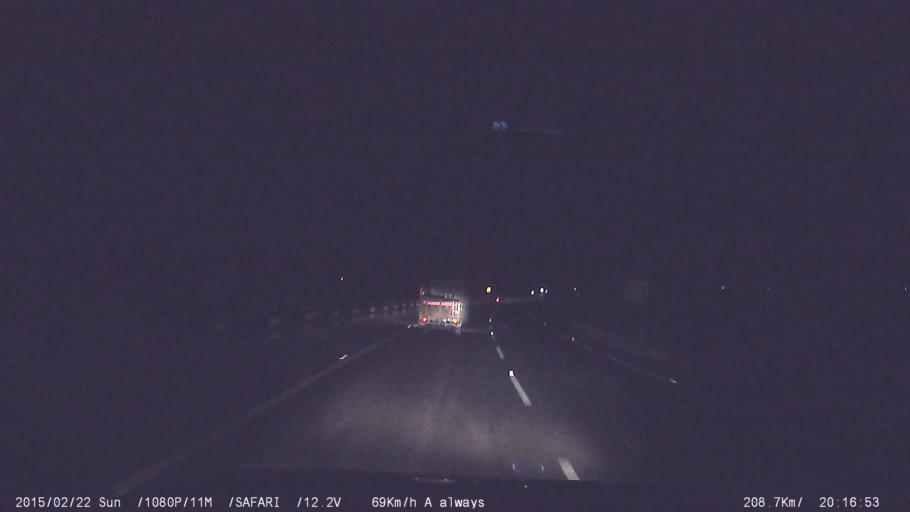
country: IN
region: Tamil Nadu
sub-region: Dindigul
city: Nilakottai
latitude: 10.2666
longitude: 77.8551
